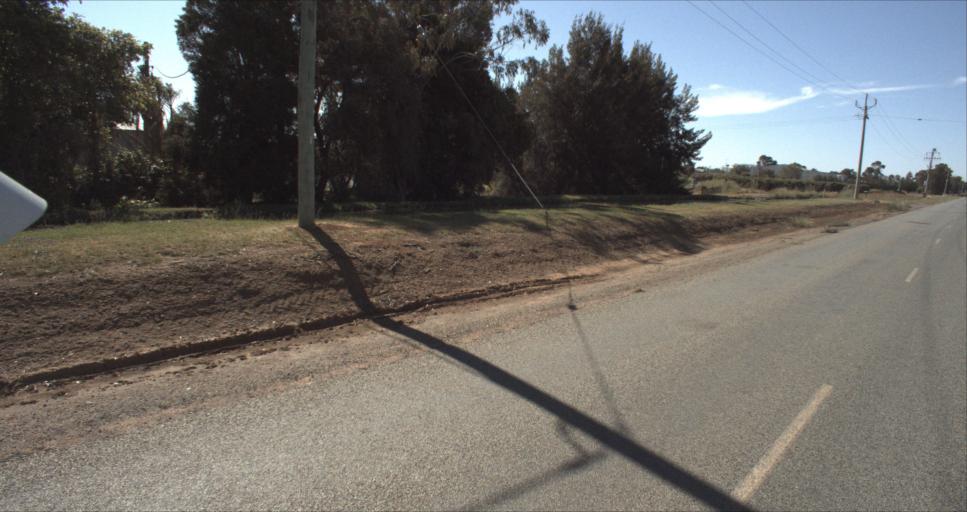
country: AU
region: New South Wales
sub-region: Leeton
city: Leeton
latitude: -34.5625
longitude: 146.3833
